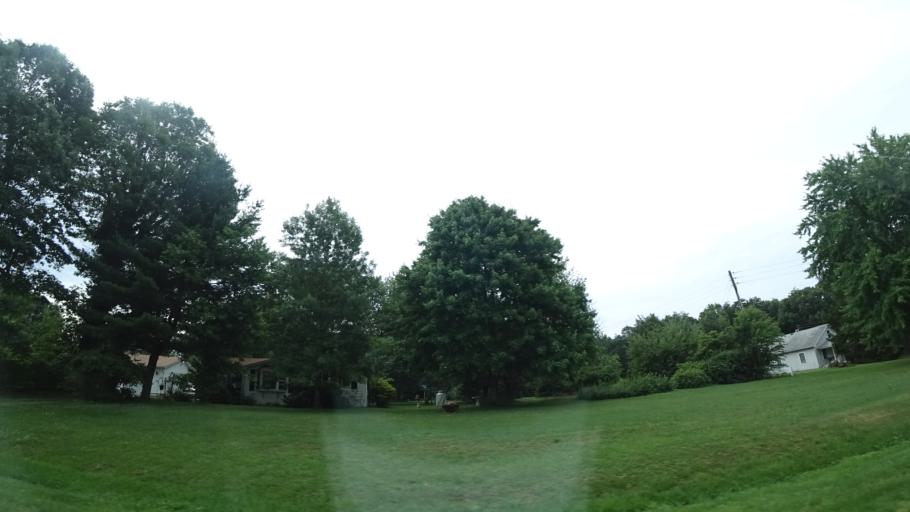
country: US
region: Virginia
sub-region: Spotsylvania County
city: Spotsylvania
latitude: 38.1401
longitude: -77.7226
